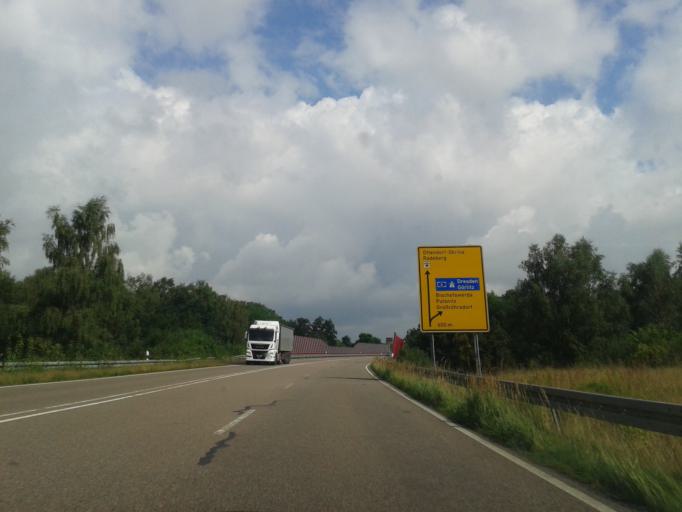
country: DE
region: Saxony
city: Radeberg
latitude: 51.1177
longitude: 13.9328
